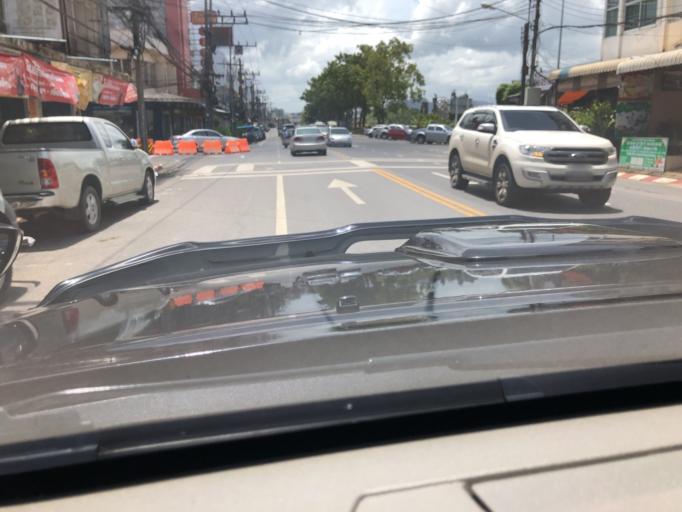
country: TH
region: Krabi
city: Krabi
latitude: 8.0634
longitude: 98.9179
